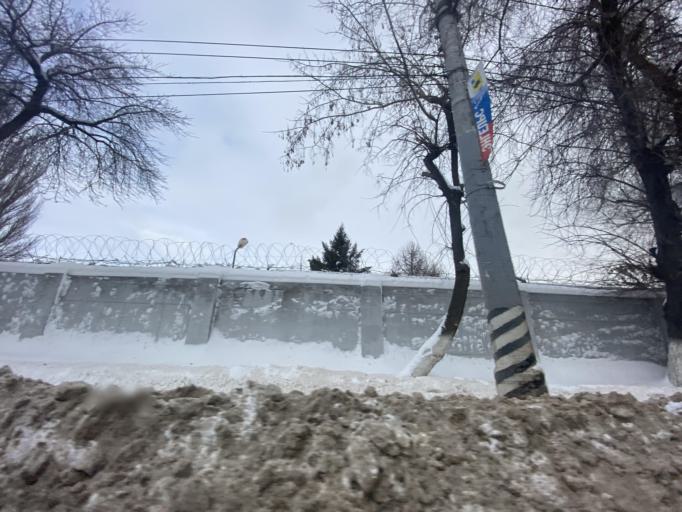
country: RU
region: Saratov
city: Engel's
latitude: 51.4969
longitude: 46.0908
